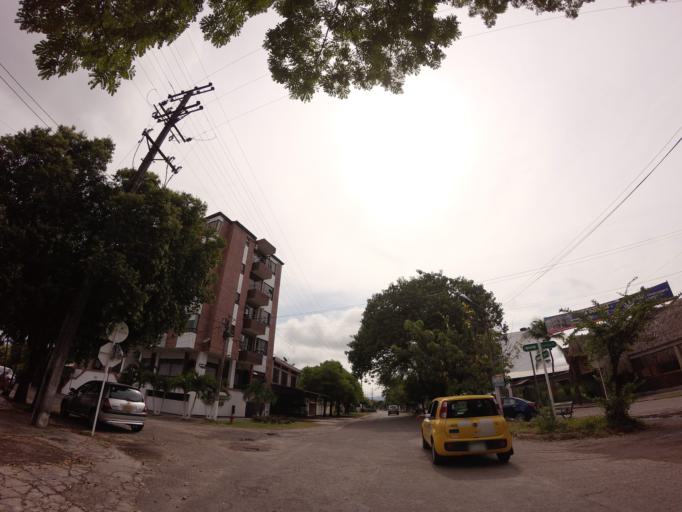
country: CO
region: Caldas
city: La Dorada
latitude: 5.4460
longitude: -74.6681
